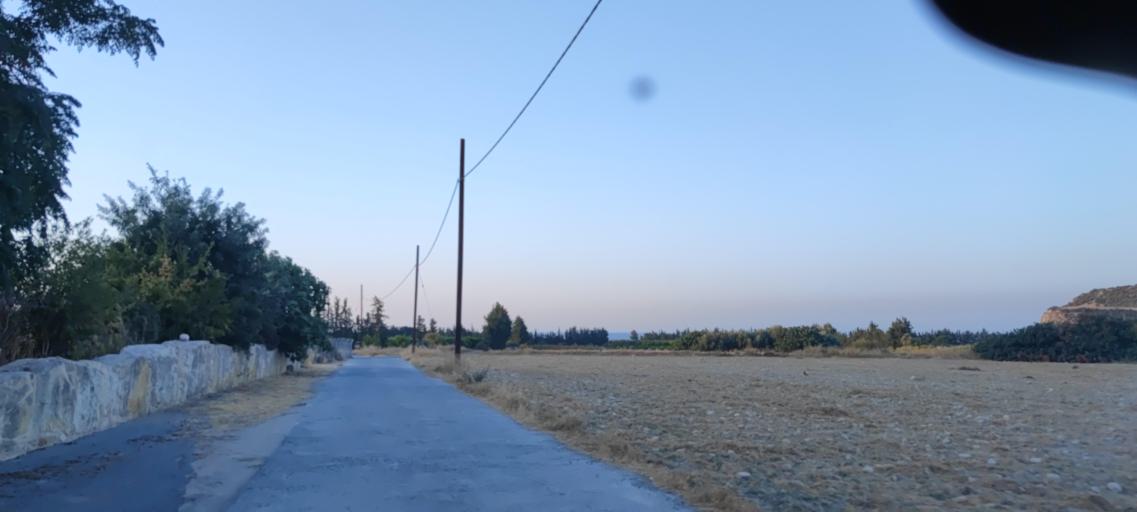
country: CY
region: Limassol
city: Sotira
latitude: 34.6749
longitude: 32.7956
